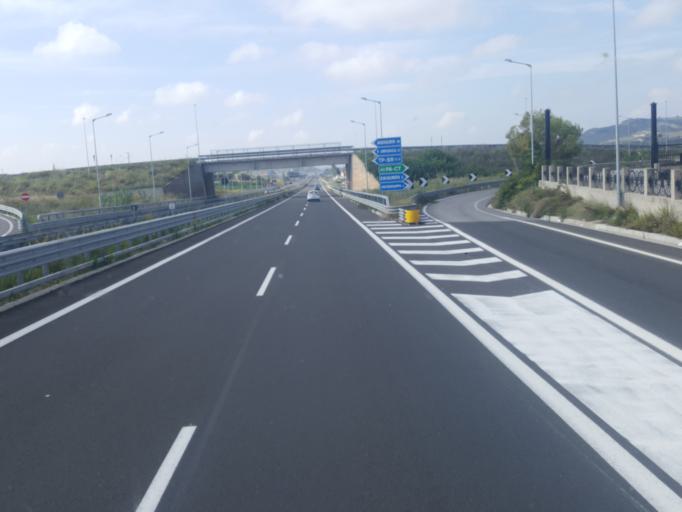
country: IT
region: Sicily
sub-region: Agrigento
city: Racalmuto
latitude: 37.3862
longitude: 13.7394
